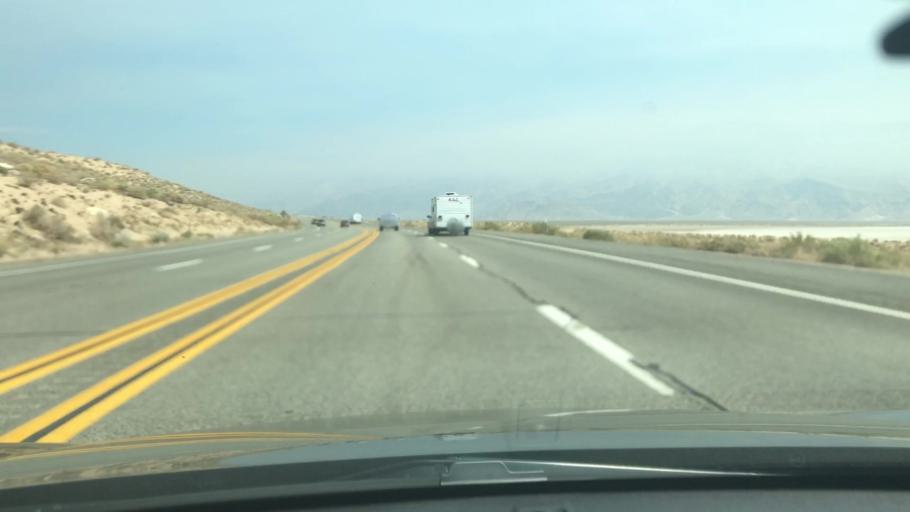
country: US
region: California
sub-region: Inyo County
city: Lone Pine
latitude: 36.5030
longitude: -118.0322
